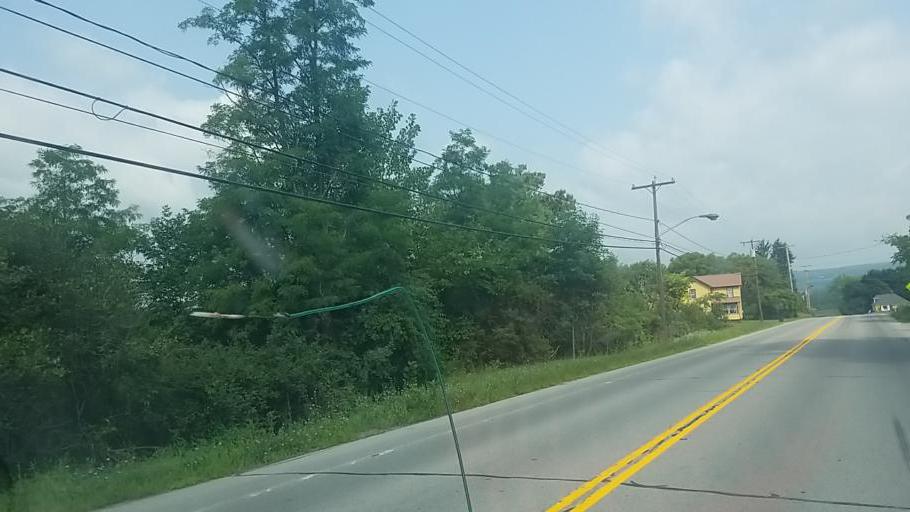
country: US
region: New York
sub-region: Montgomery County
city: Fort Plain
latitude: 42.9526
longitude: -74.6206
